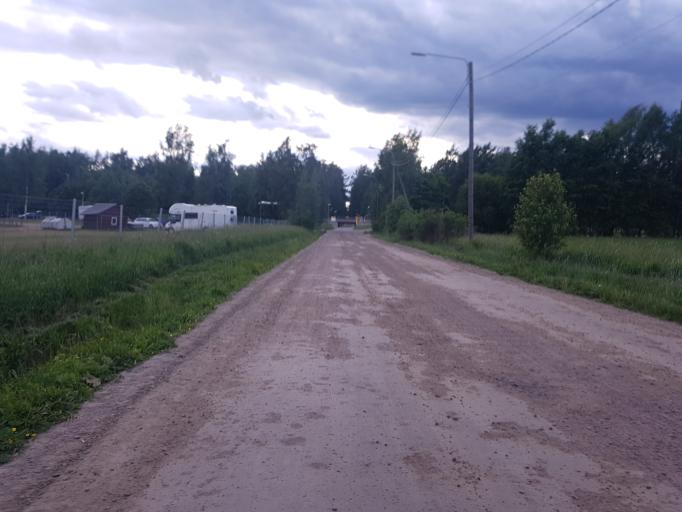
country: FI
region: Uusimaa
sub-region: Helsinki
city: Vantaa
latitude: 60.2563
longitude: 24.9618
